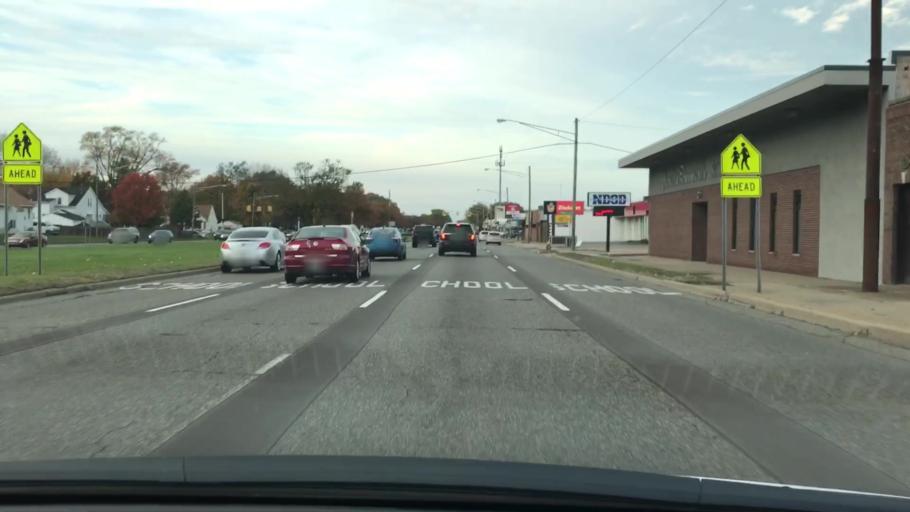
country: US
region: Michigan
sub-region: Wayne County
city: Inkster
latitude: 42.2865
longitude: -83.2708
